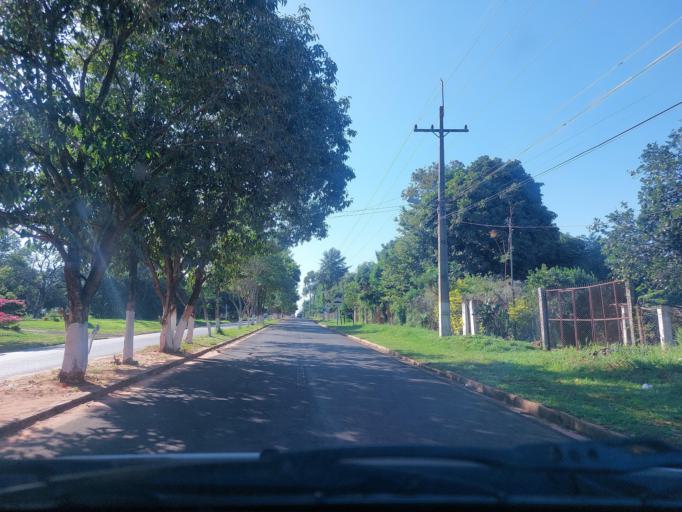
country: PY
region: San Pedro
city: Guayaybi
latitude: -24.5316
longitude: -56.4517
